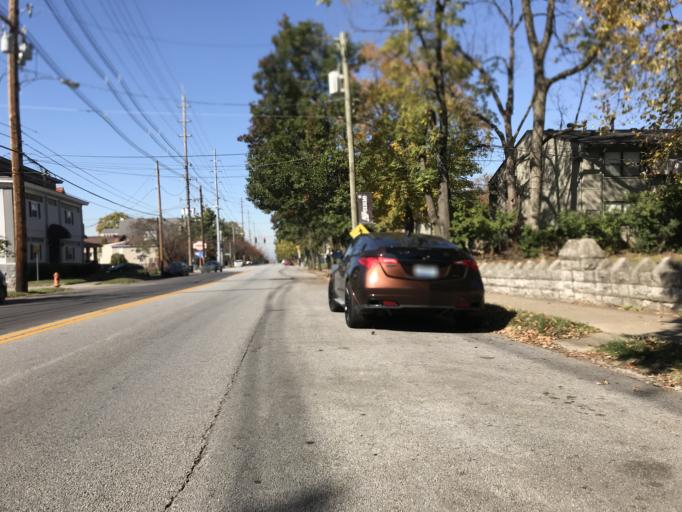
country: US
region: Indiana
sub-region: Clark County
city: Jeffersonville
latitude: 38.2551
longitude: -85.7116
